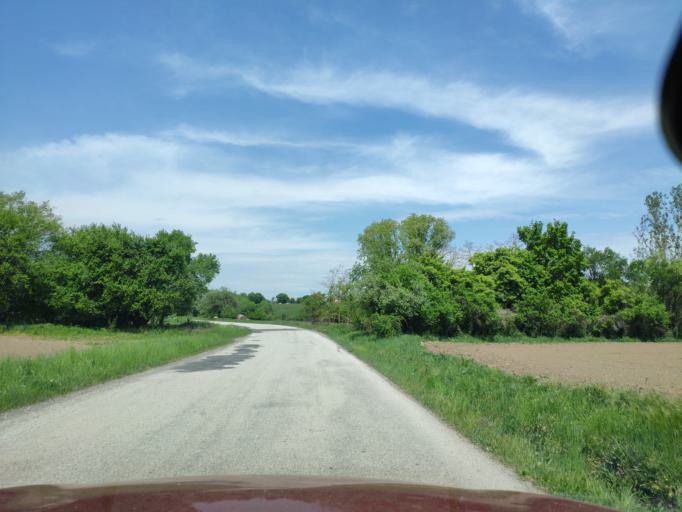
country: SK
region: Banskobystricky
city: Rimavska Sobota
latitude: 48.4618
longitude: 20.1050
